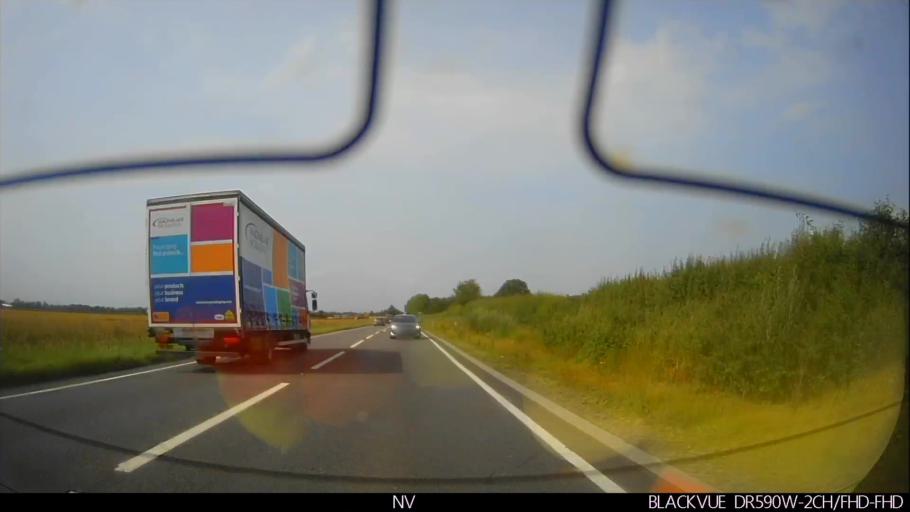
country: GB
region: England
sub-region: City of York
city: Holtby
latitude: 54.0096
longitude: -0.9993
